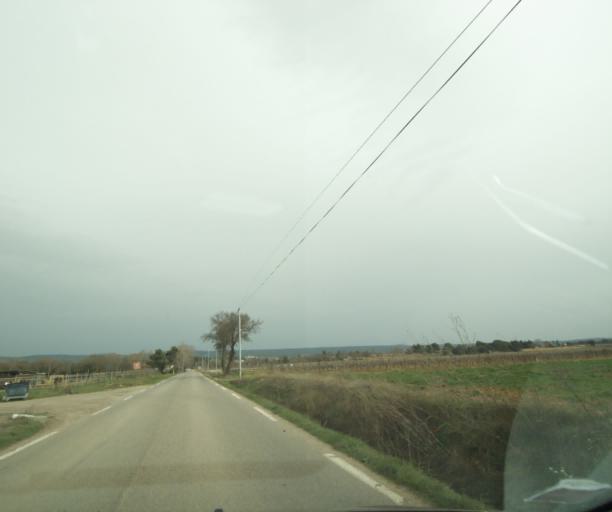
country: FR
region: Provence-Alpes-Cote d'Azur
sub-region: Departement du Var
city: Pourrieres
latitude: 43.4811
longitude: 5.7176
